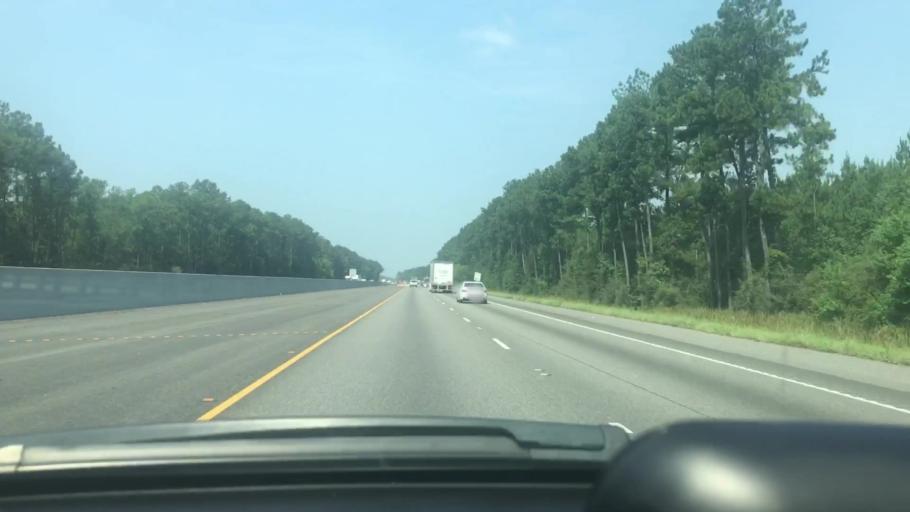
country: US
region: Louisiana
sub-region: Livingston Parish
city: Livingston
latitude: 30.4741
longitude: -90.7770
